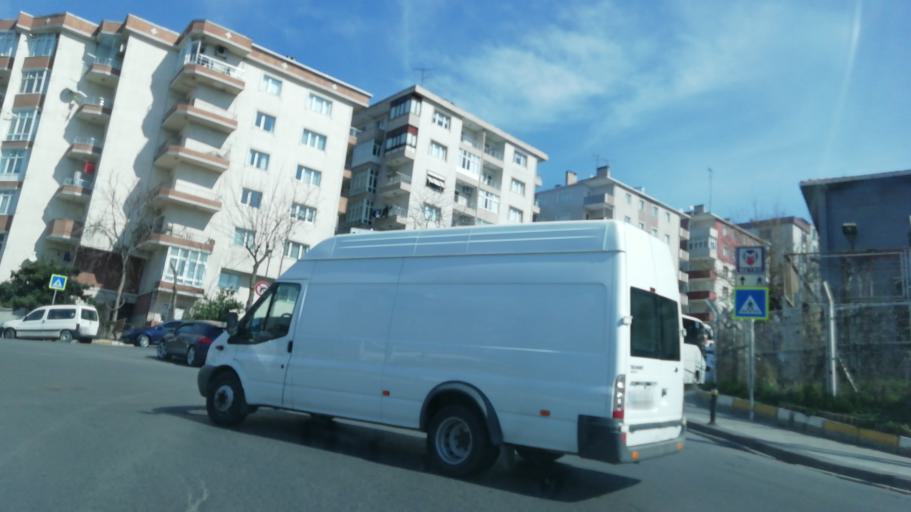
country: TR
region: Istanbul
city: Bagcilar
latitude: 41.0335
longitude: 28.8531
